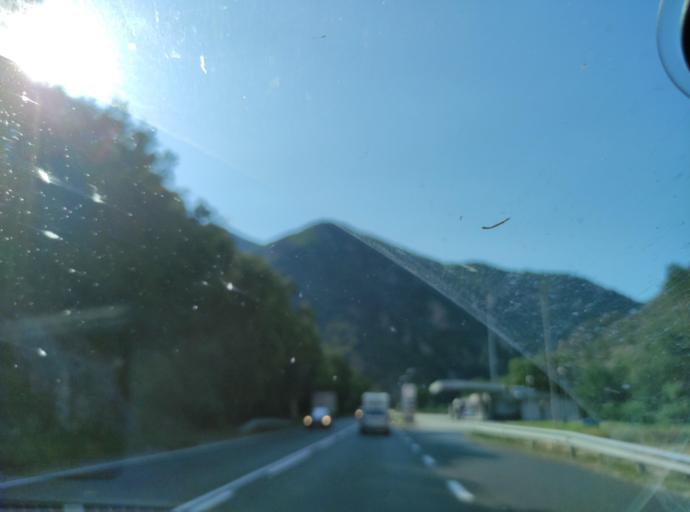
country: BG
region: Blagoevgrad
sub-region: Obshtina Kresna
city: Stara Kresna
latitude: 41.8124
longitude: 23.1611
